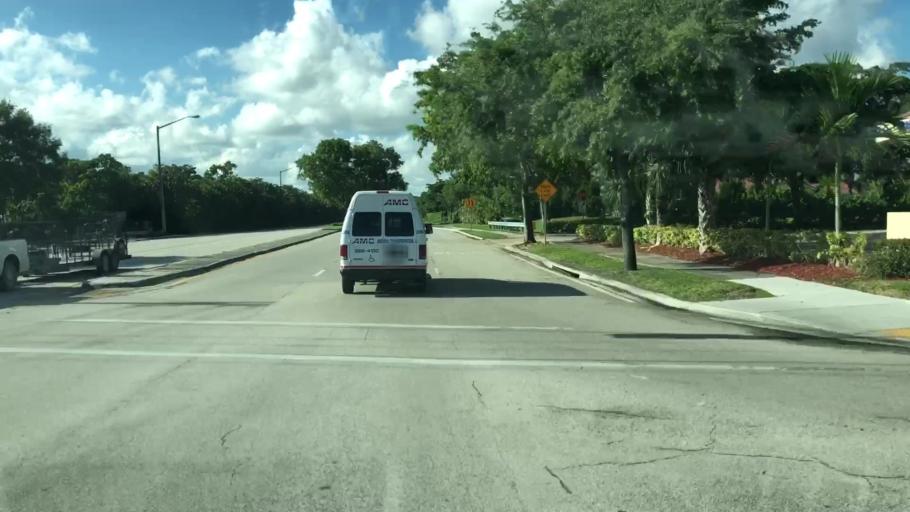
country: US
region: Florida
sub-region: Broward County
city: Coral Springs
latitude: 26.2588
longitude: -80.2661
